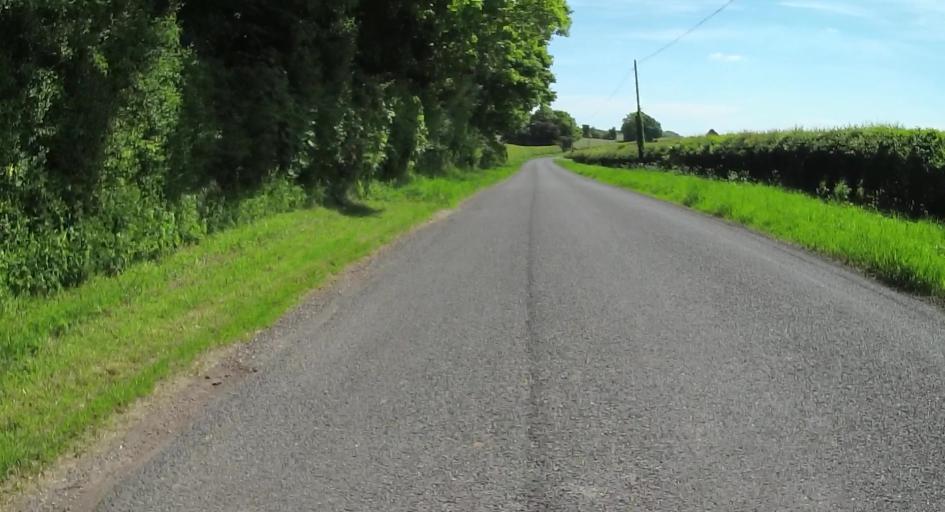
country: GB
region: England
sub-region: Hampshire
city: Four Marks
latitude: 51.1639
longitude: -1.1361
